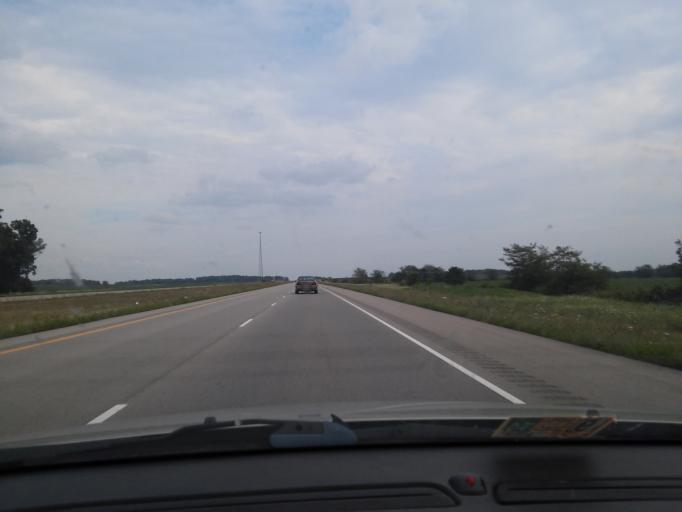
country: US
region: Ohio
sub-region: Ross County
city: Frankfort
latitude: 39.4790
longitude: -83.2829
